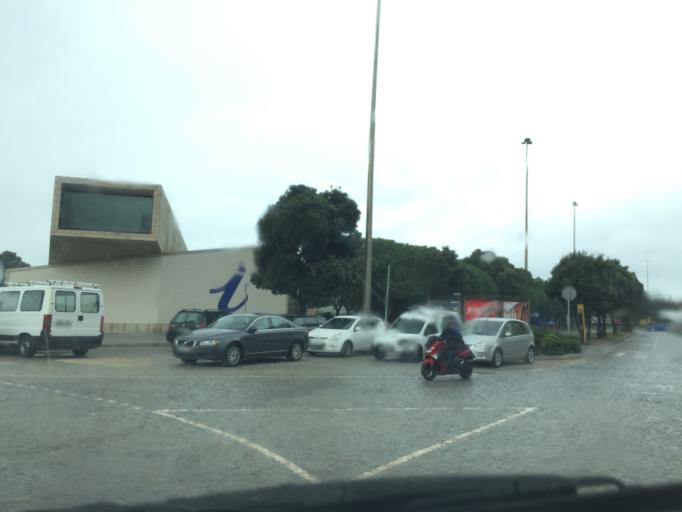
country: PT
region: Porto
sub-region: Matosinhos
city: Matosinhos
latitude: 41.1799
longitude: -8.6932
